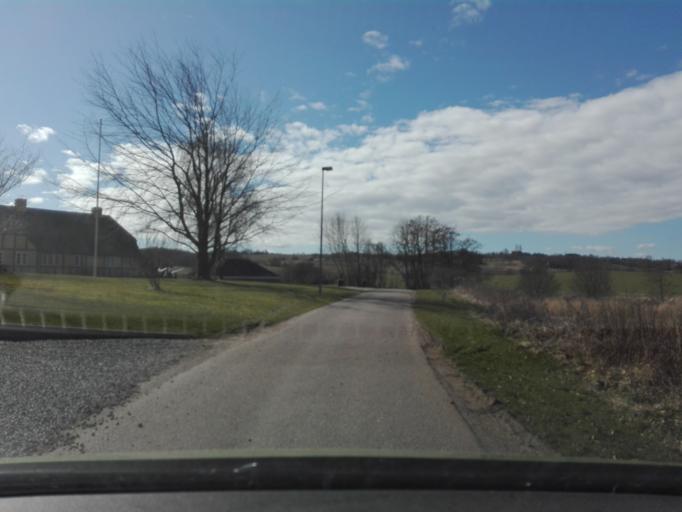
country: DK
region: Central Jutland
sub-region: Horsens Kommune
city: Horsens
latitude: 55.8861
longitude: 9.9598
